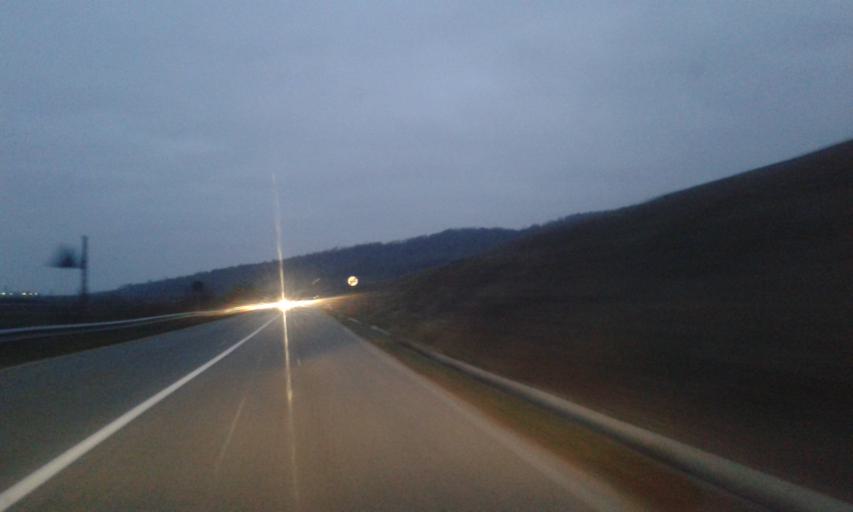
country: RO
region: Gorj
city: Targu Jiu
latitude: 45.0684
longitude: 23.2822
